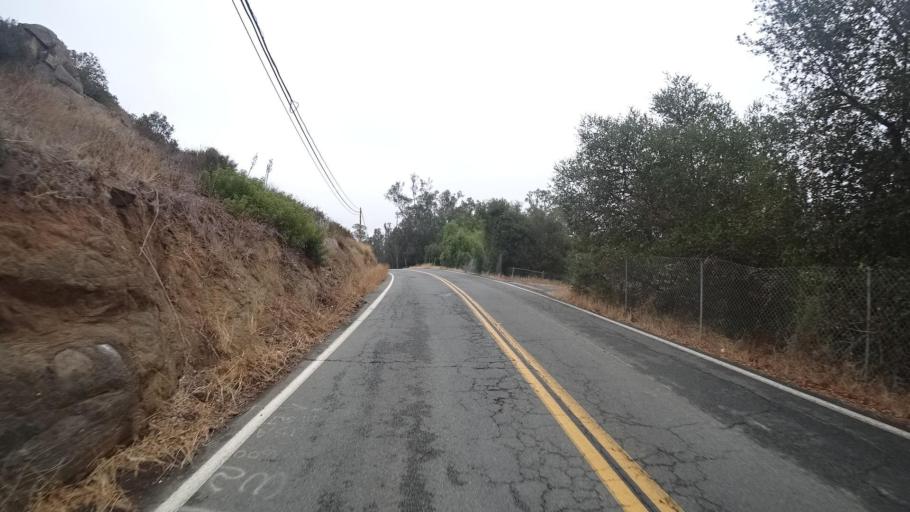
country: US
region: California
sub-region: San Diego County
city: Escondido
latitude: 33.1033
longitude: -117.1231
